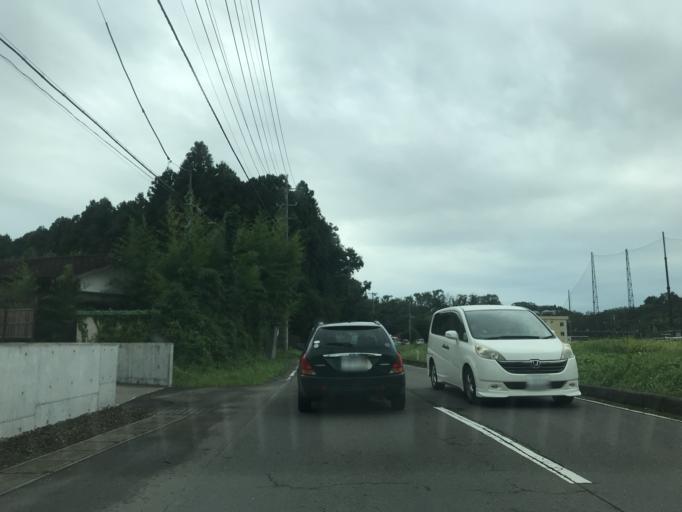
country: JP
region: Miyagi
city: Sendai-shi
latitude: 38.3194
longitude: 140.8645
